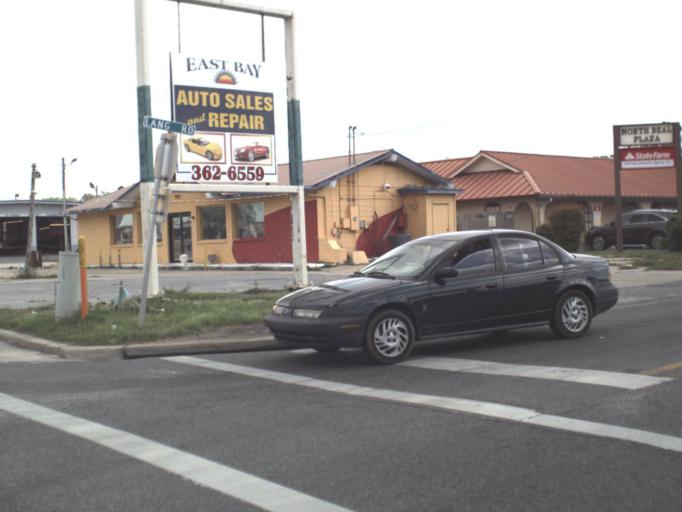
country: US
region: Florida
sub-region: Okaloosa County
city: Wright
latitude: 30.4362
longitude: -86.6387
